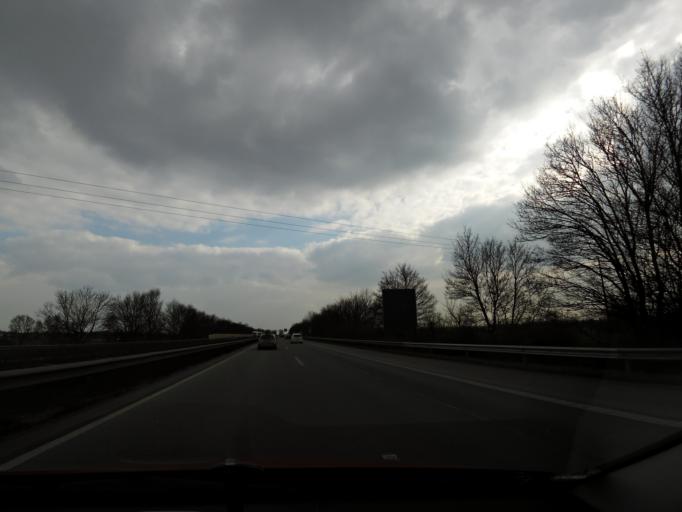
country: DE
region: Rheinland-Pfalz
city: Beindersheim
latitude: 49.5630
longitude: 8.3067
